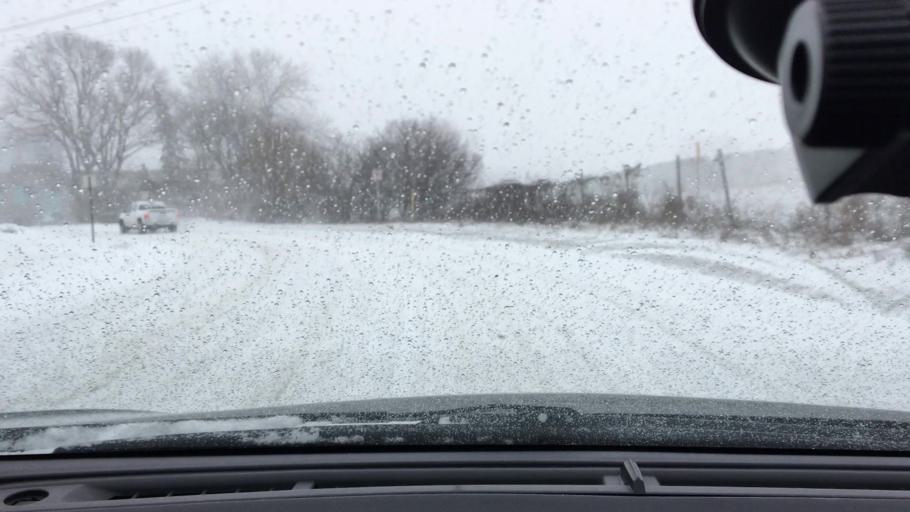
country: US
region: Minnesota
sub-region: Hennepin County
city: New Hope
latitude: 44.9847
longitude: -93.4000
